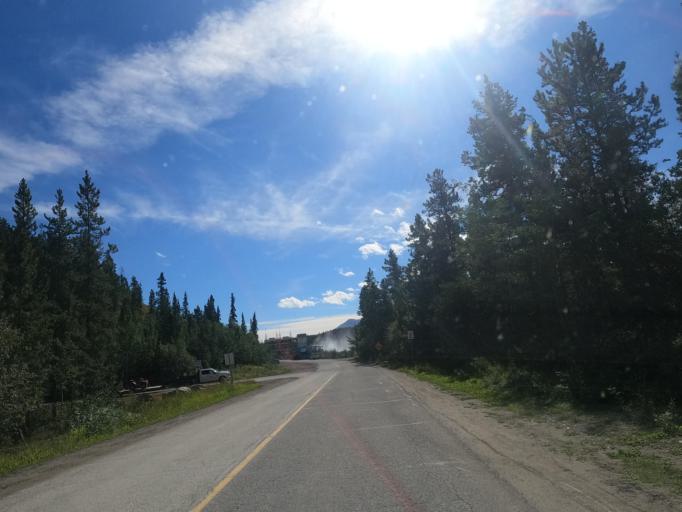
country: CA
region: Yukon
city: Whitehorse
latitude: 60.6981
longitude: -135.0409
